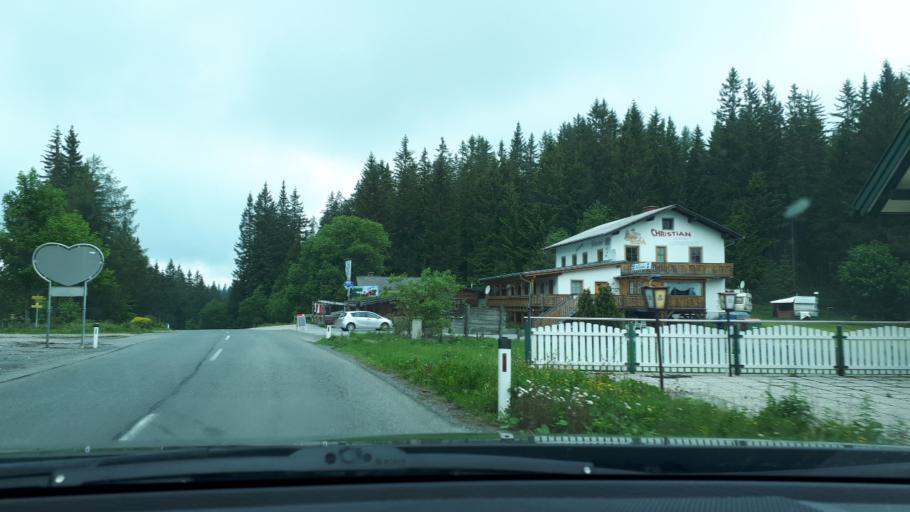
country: AT
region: Styria
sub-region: Politischer Bezirk Voitsberg
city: Modriach
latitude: 46.9299
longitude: 15.0069
